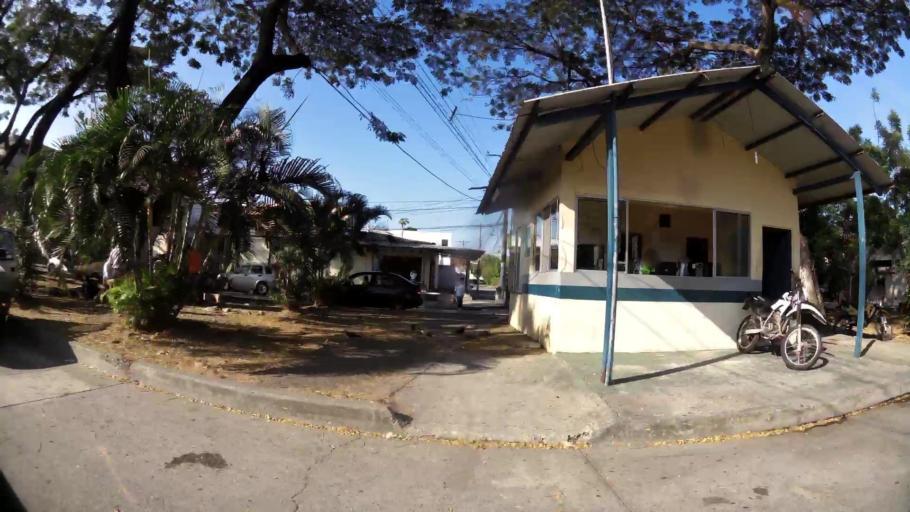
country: EC
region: Guayas
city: Eloy Alfaro
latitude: -2.1694
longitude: -79.8858
